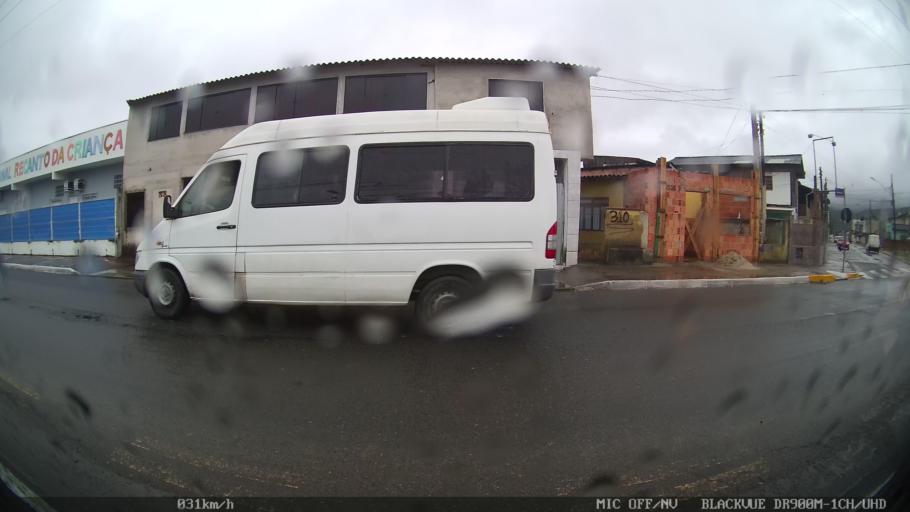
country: BR
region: Santa Catarina
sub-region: Itajai
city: Itajai
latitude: -26.9226
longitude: -48.6971
